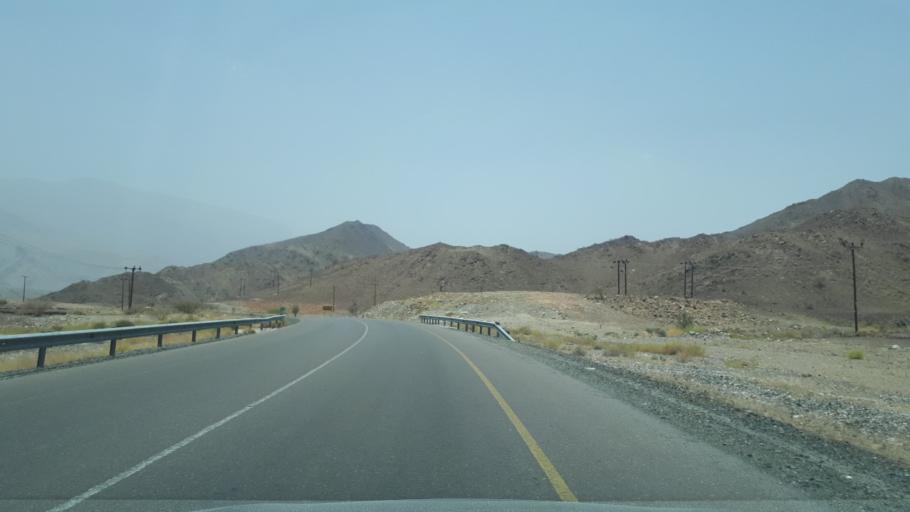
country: OM
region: Al Batinah
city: Rustaq
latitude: 23.4047
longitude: 57.2434
